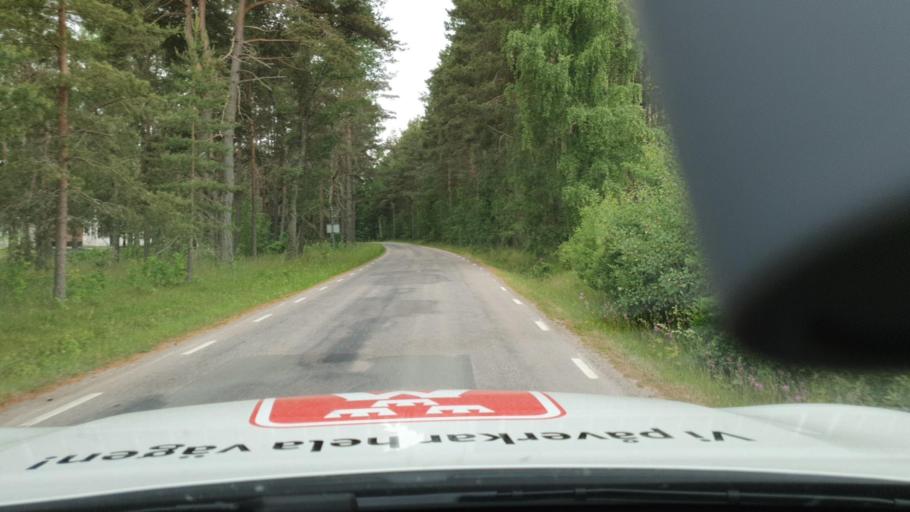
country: SE
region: Vaestra Goetaland
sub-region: Hjo Kommun
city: Hjo
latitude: 58.1828
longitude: 14.2008
